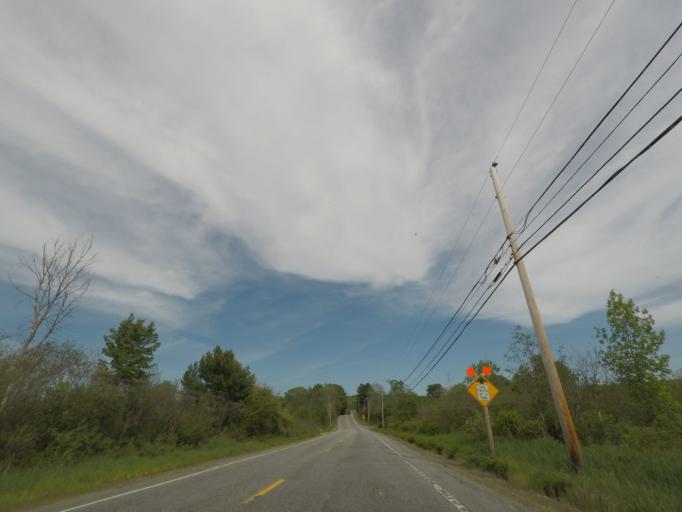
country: US
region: Maine
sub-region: Sagadahoc County
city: Richmond
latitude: 44.0848
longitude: -69.7533
